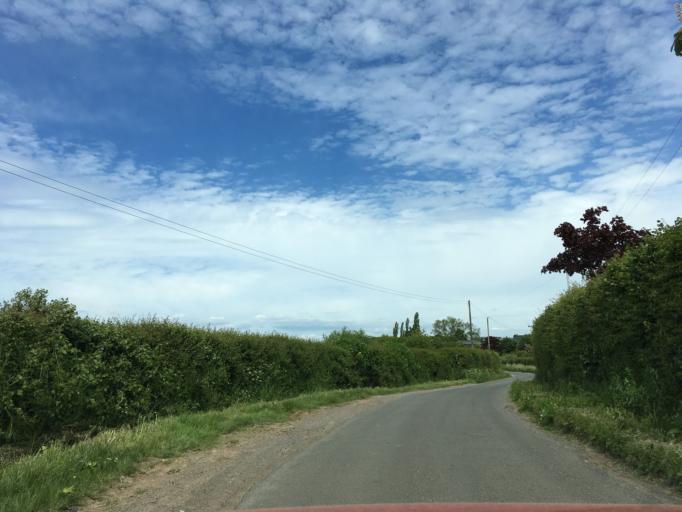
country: GB
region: England
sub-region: South Gloucestershire
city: Charfield
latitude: 51.6641
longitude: -2.4110
